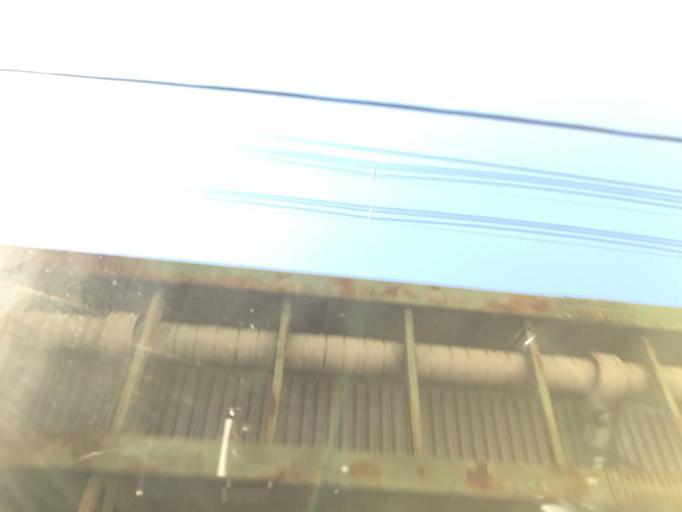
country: US
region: Massachusetts
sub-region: Essex County
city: South Peabody
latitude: 42.5231
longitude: -70.9820
